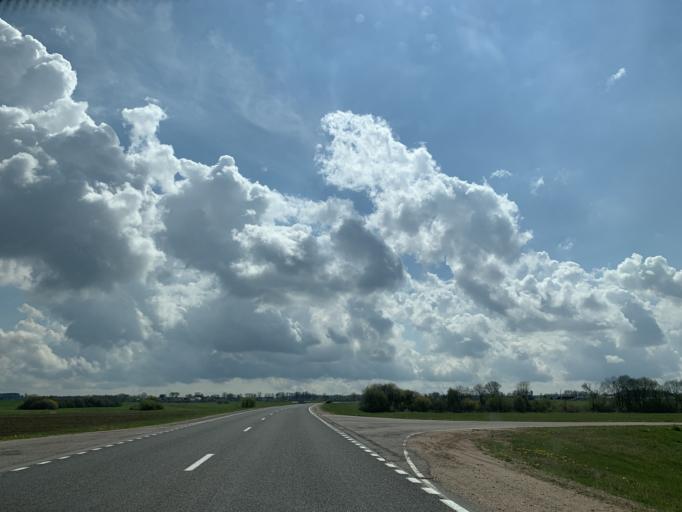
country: BY
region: Minsk
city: Nyasvizh
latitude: 53.2366
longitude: 26.7165
